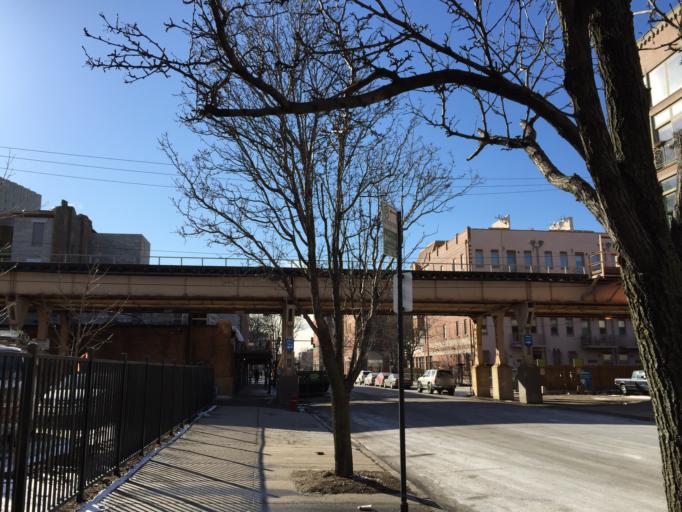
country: US
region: Illinois
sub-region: Cook County
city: Chicago
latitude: 41.8554
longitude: -87.6260
